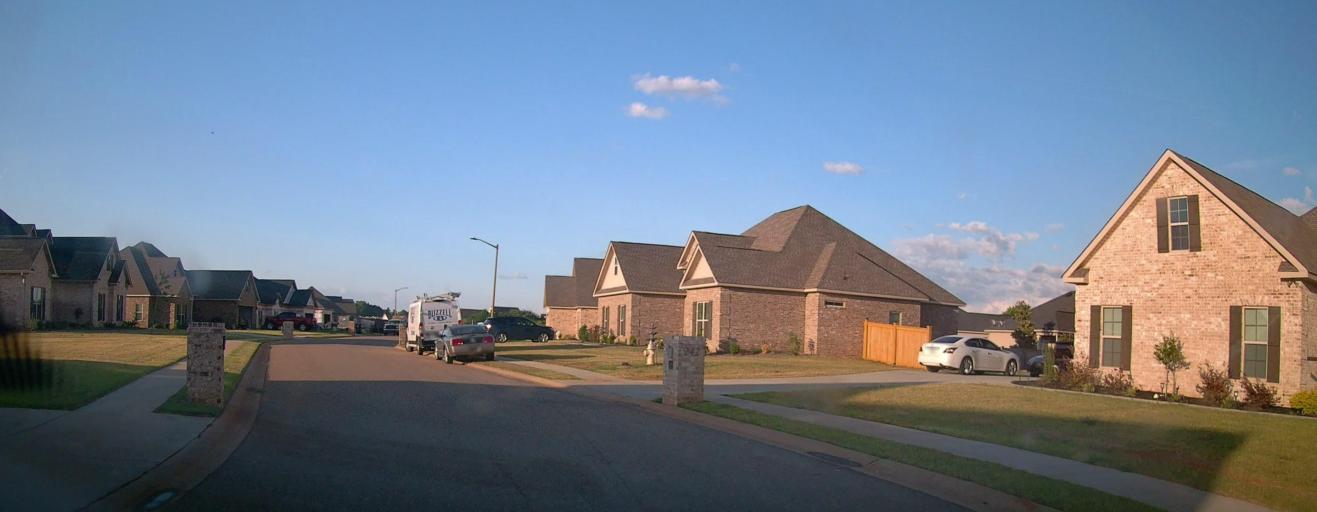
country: US
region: Georgia
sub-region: Houston County
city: Centerville
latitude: 32.6288
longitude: -83.7204
